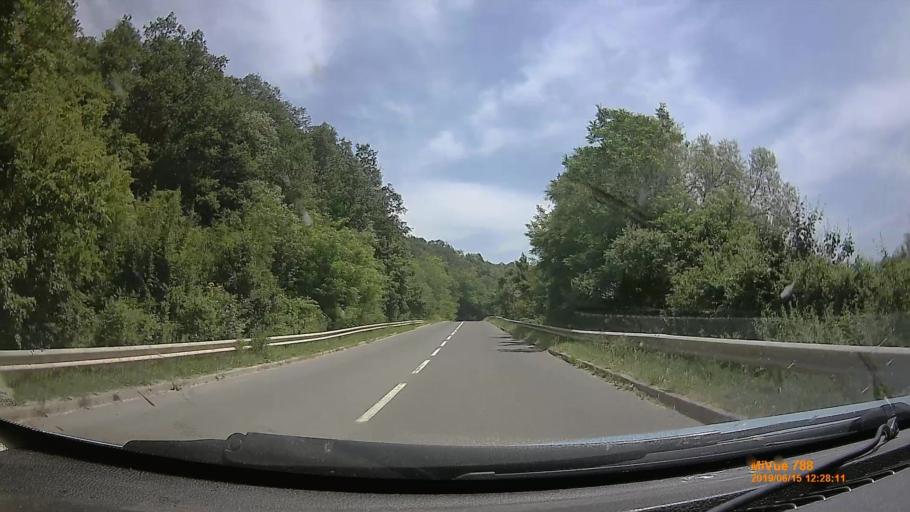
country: HU
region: Baranya
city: Buekkoesd
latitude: 46.1278
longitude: 18.0221
